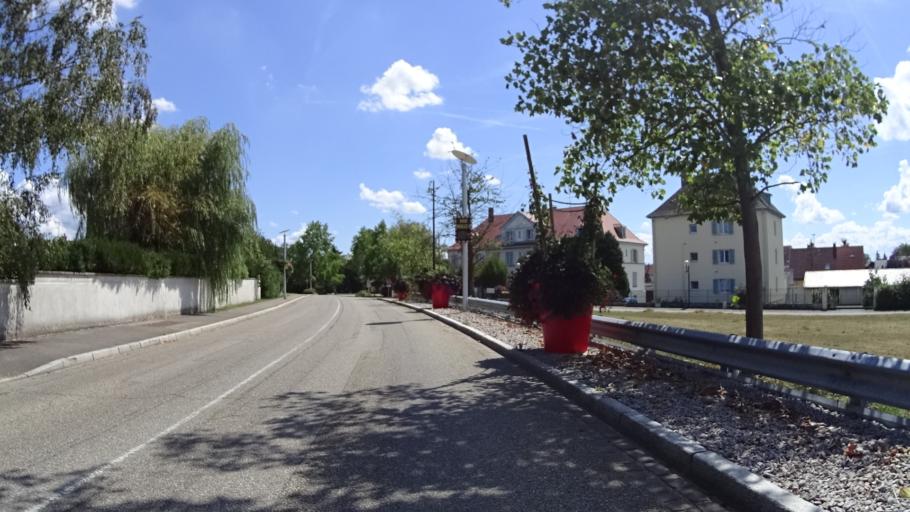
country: FR
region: Alsace
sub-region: Departement du Haut-Rhin
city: Ottmarsheim
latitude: 47.7921
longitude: 7.5042
